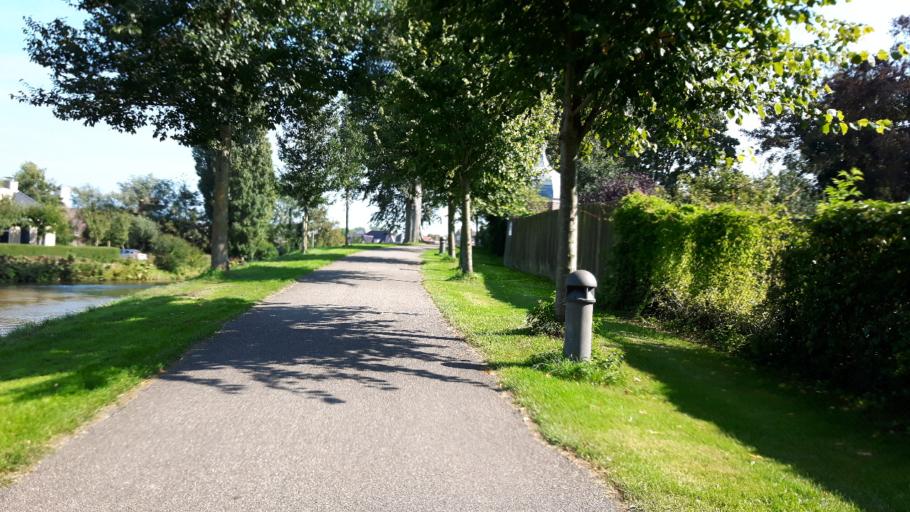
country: NL
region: Friesland
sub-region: Gemeente Franekeradeel
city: Franeker
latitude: 53.1883
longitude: 5.5463
